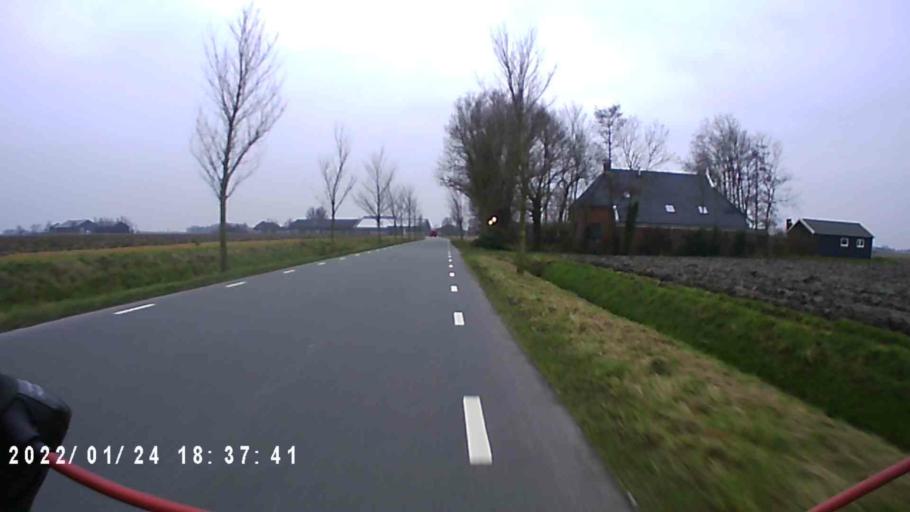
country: NL
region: Groningen
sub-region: Gemeente De Marne
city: Ulrum
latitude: 53.3508
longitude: 6.3360
